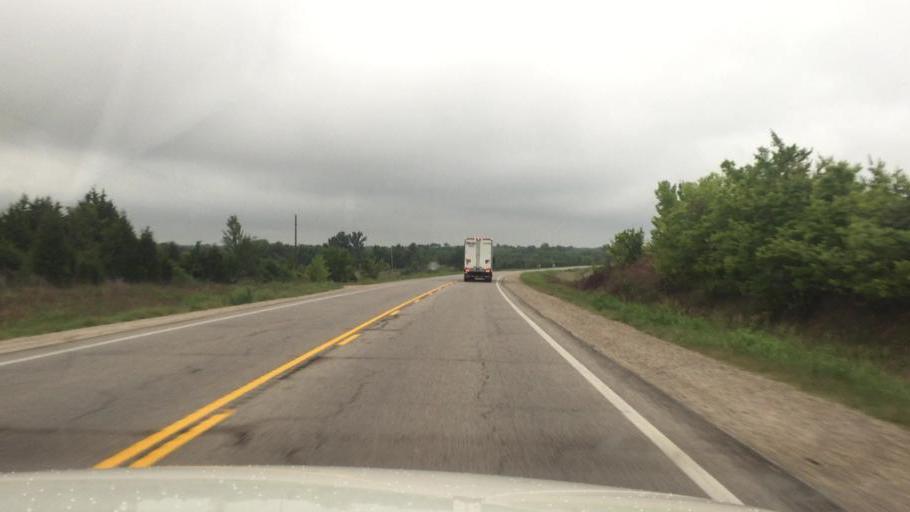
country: US
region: Kansas
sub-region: Montgomery County
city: Coffeyville
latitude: 37.1403
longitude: -95.5768
